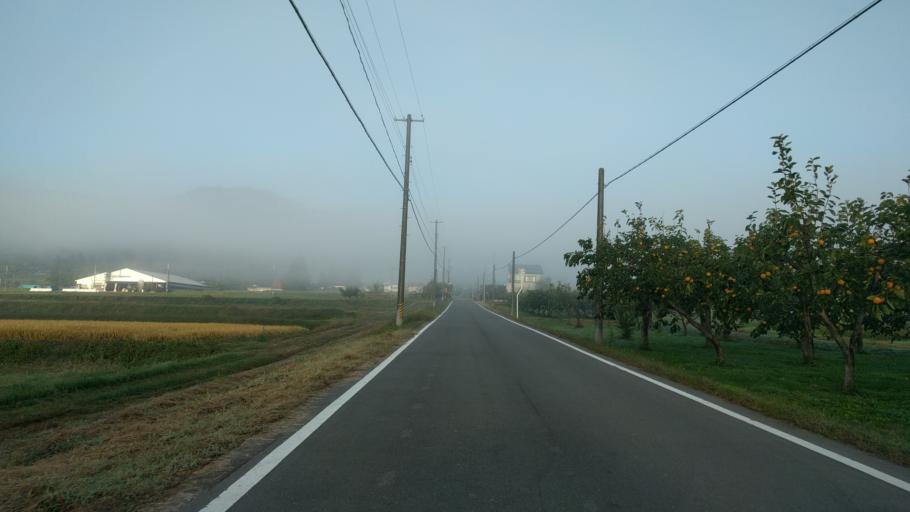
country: JP
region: Fukushima
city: Kitakata
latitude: 37.4455
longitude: 139.8084
